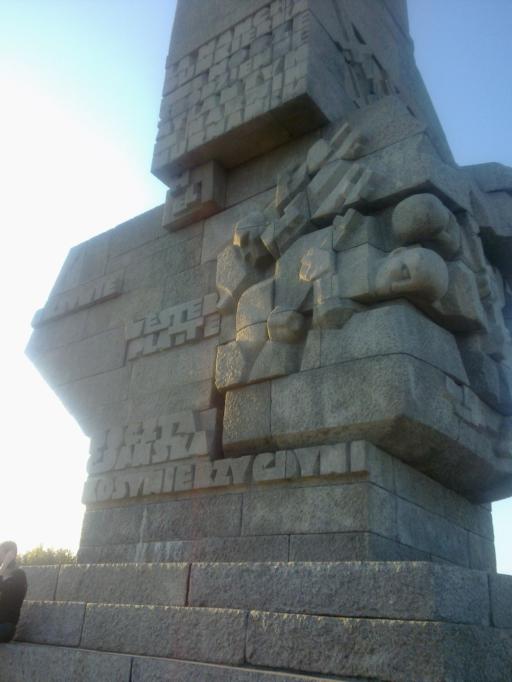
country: PL
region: Pomeranian Voivodeship
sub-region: Gdansk
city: Gdansk
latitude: 54.4066
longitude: 18.6670
